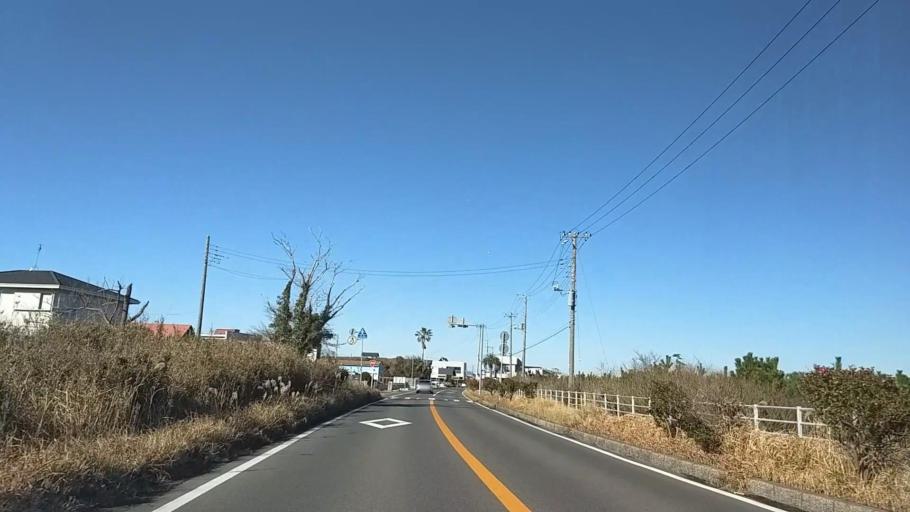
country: JP
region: Chiba
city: Ohara
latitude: 35.3511
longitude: 140.3898
